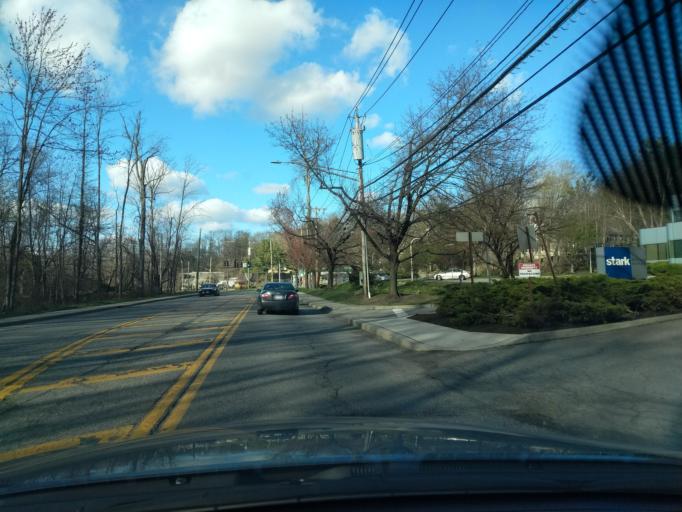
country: US
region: New York
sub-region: Westchester County
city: Mount Kisco
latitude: 41.2115
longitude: -73.7221
